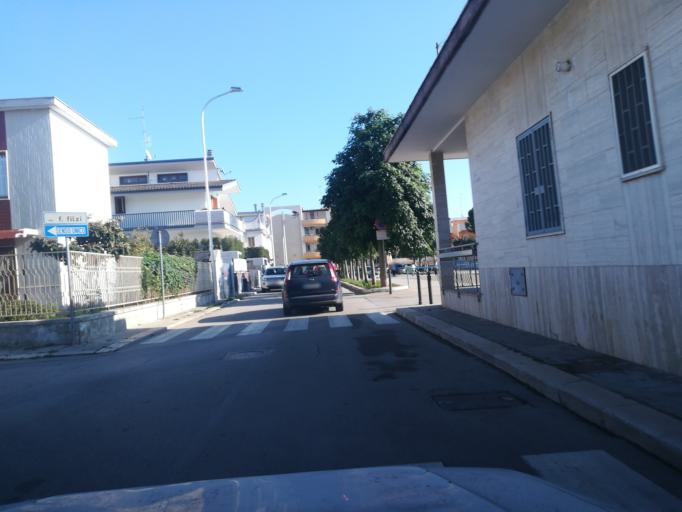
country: IT
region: Apulia
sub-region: Provincia di Bari
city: Modugno
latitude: 41.0779
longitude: 16.7772
